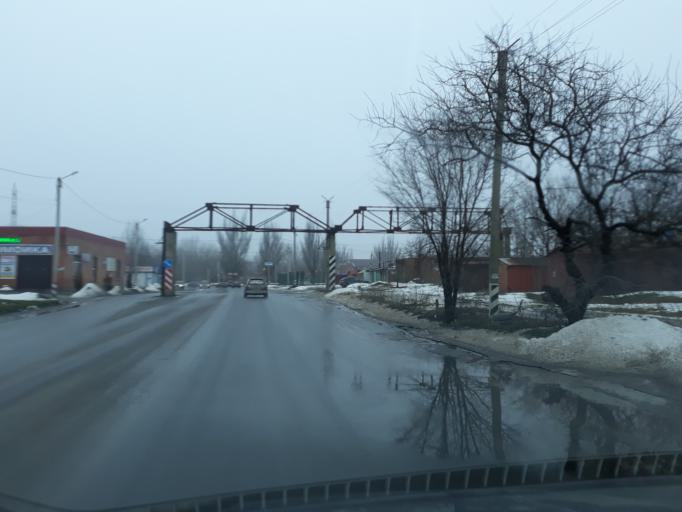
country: RU
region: Rostov
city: Novobessergenovka
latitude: 47.2122
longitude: 38.8652
